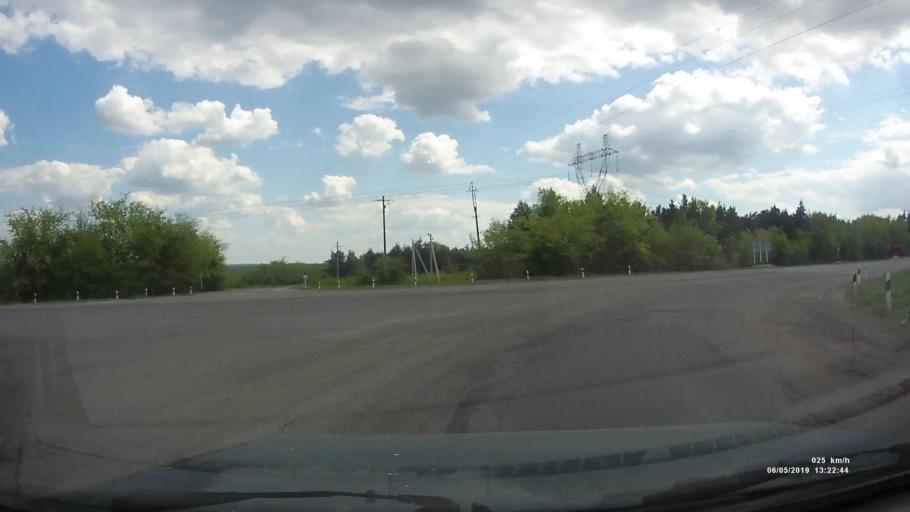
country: RU
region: Rostov
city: Ust'-Donetskiy
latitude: 47.6942
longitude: 40.9231
